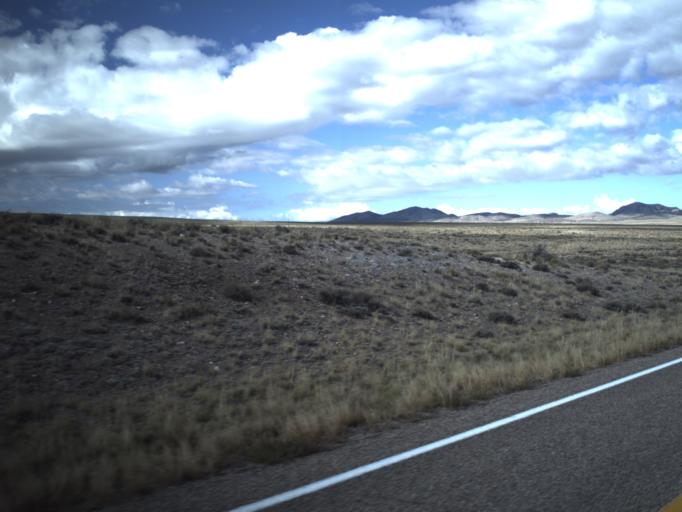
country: US
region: Utah
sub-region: Beaver County
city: Milford
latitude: 38.4335
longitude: -113.1334
